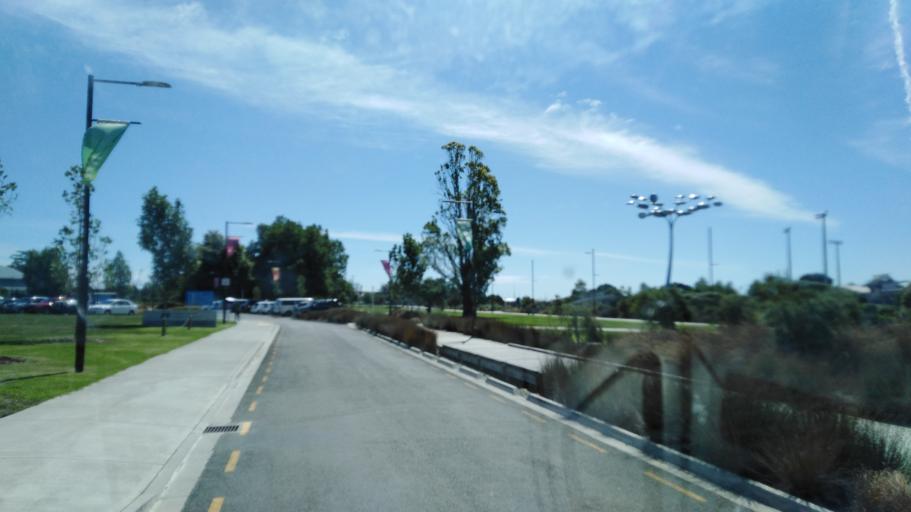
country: NZ
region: Nelson
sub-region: Nelson City
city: Nelson
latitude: -41.2689
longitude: 173.2814
